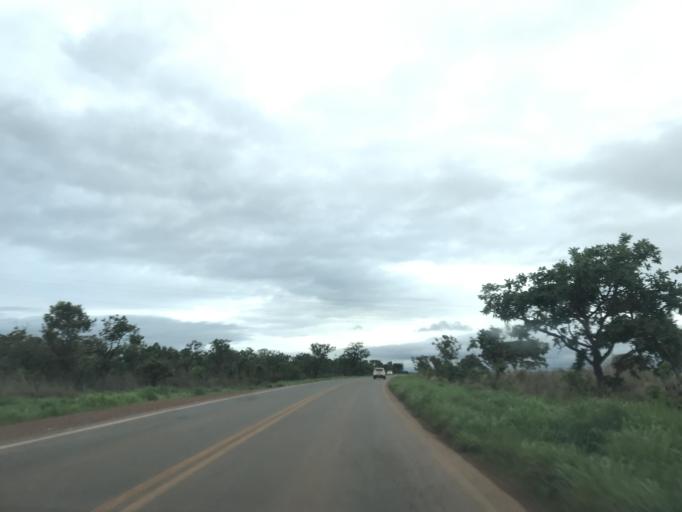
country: BR
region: Goias
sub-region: Luziania
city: Luziania
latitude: -16.2935
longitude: -48.0074
